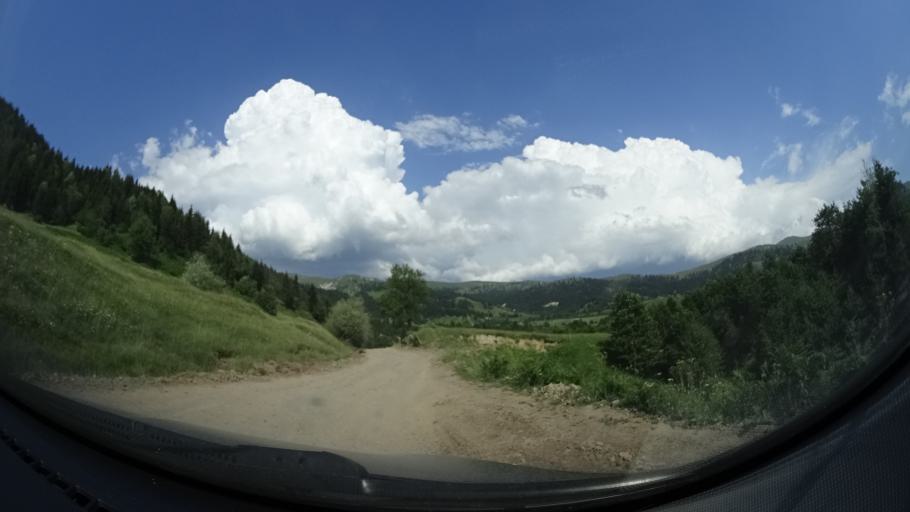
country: GE
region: Ajaria
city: Dioknisi
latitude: 41.6471
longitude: 42.4778
